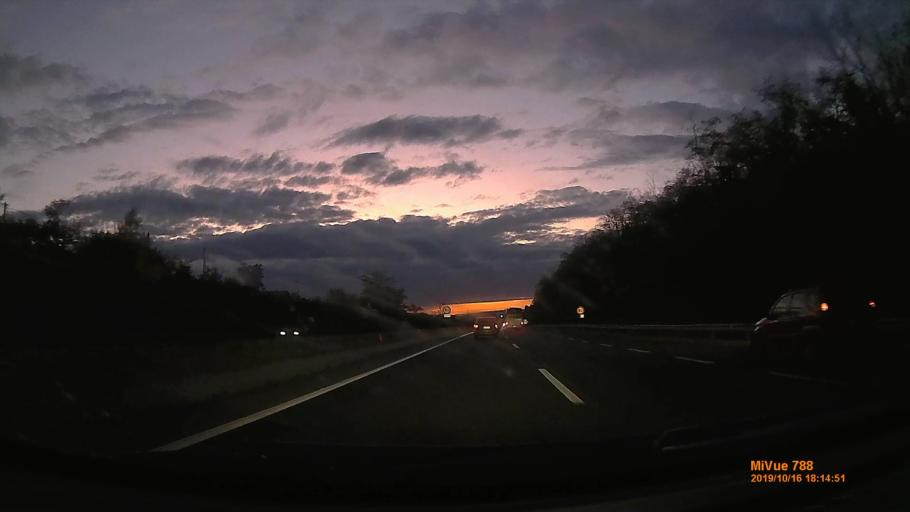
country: HU
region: Pest
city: Mogyorod
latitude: 47.6013
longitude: 19.2690
